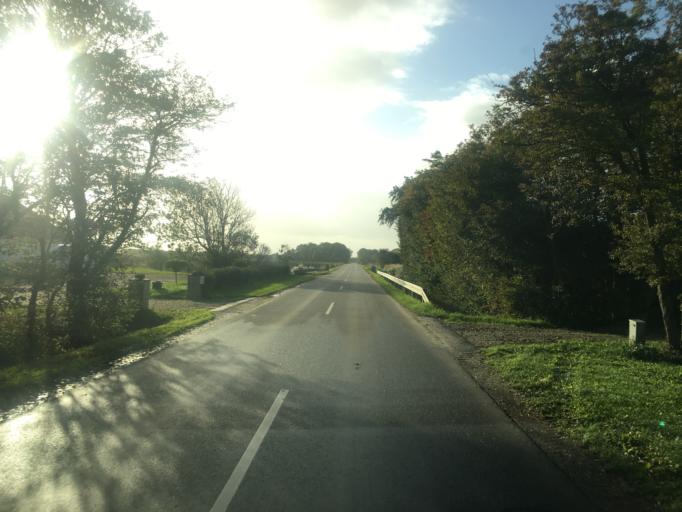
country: DE
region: Schleswig-Holstein
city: Aventoft
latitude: 54.9219
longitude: 8.7957
